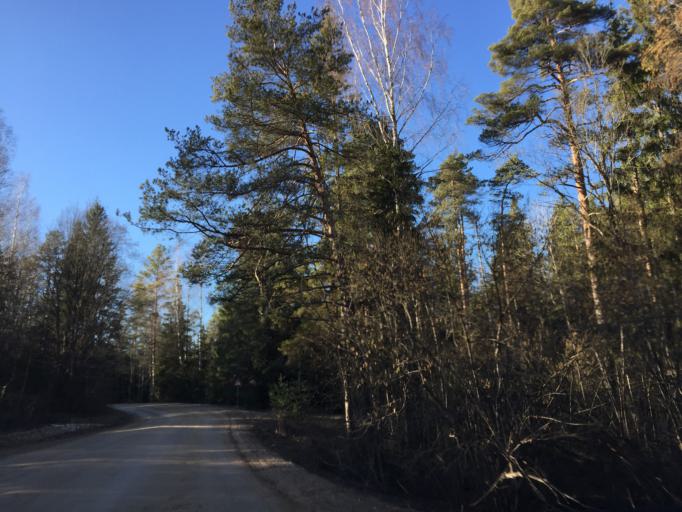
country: LV
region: Ropazu
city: Ropazi
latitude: 56.9185
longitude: 24.7118
